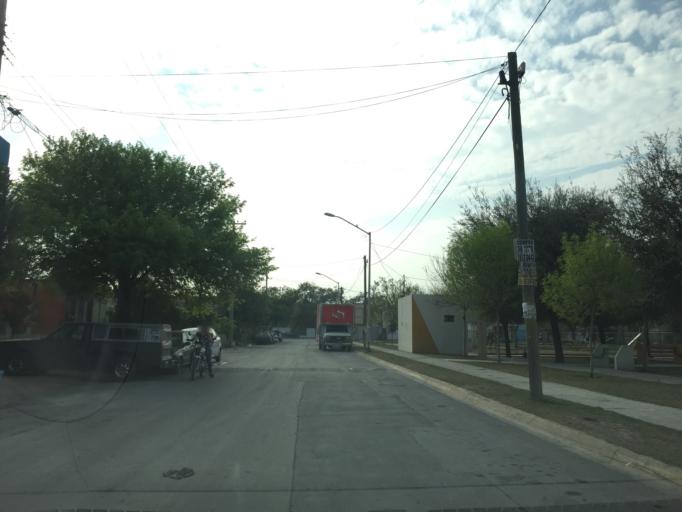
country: MX
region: Nuevo Leon
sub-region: Apodaca
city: Fraccionamiento Cosmopolis Octavo Sector
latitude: 25.8121
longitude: -100.2541
